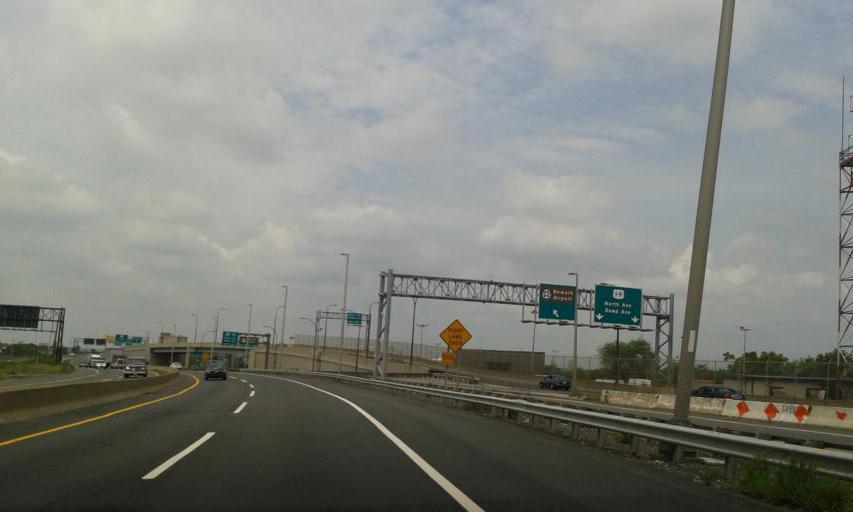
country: US
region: New Jersey
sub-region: Union County
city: Elizabeth
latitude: 40.6725
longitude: -74.1858
